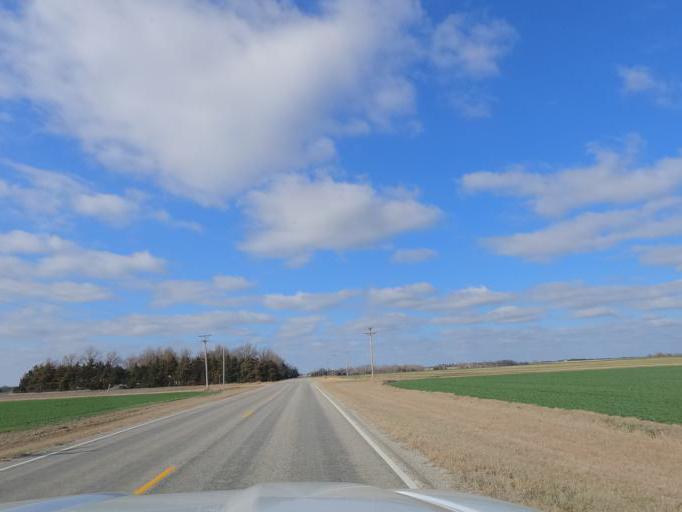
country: US
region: Kansas
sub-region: McPherson County
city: Inman
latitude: 38.2024
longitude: -97.8490
